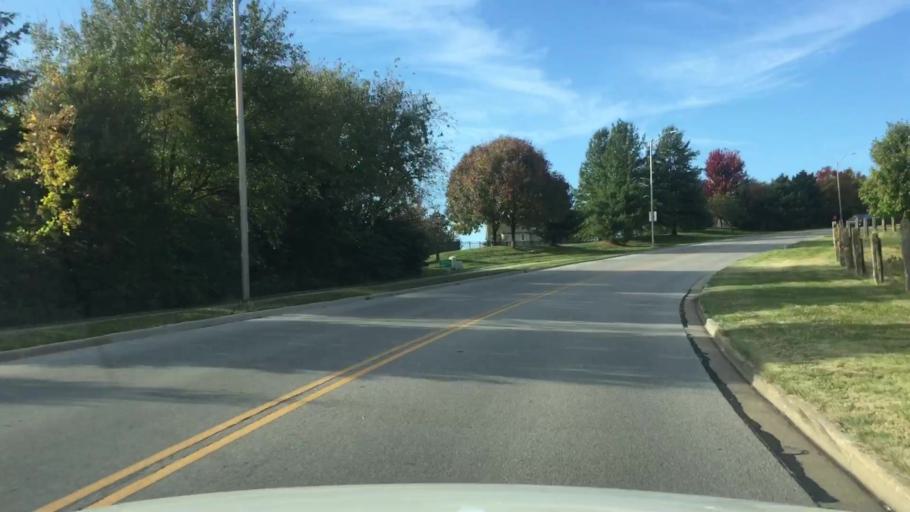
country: US
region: Kansas
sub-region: Johnson County
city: Shawnee
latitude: 39.0328
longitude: -94.7493
